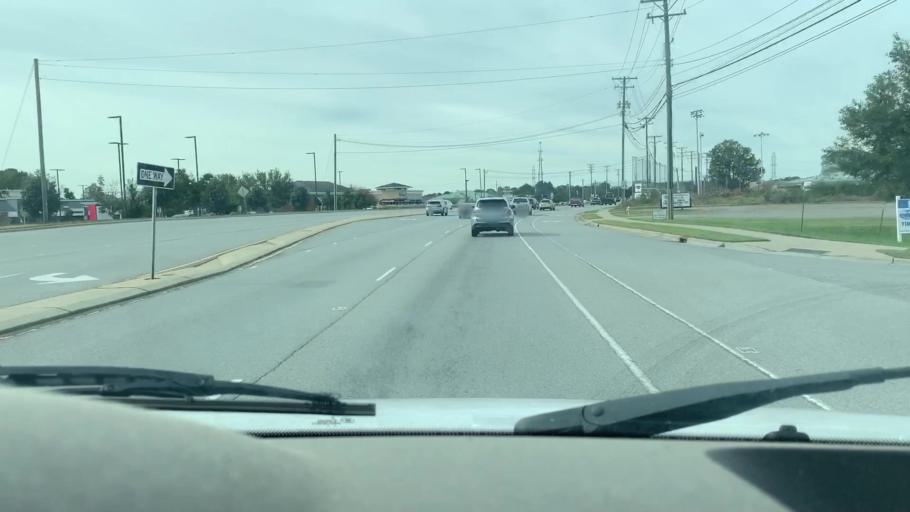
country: US
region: North Carolina
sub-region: Iredell County
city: Mooresville
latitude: 35.5834
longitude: -80.8749
